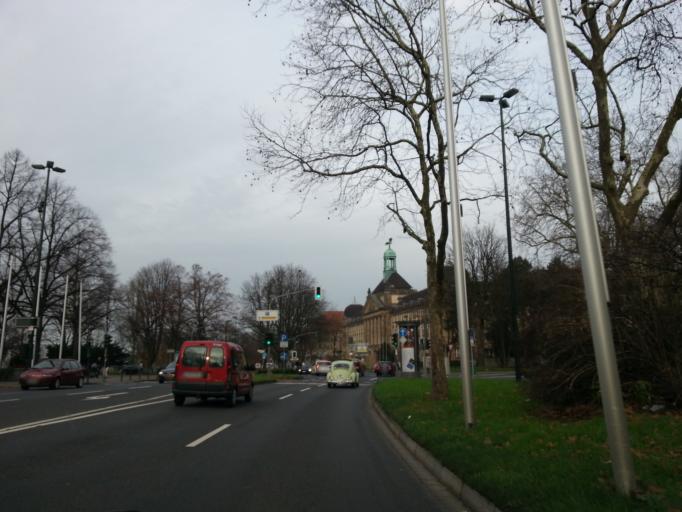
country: DE
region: North Rhine-Westphalia
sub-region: Regierungsbezirk Dusseldorf
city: Dusseldorf
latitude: 51.2359
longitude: 6.7718
